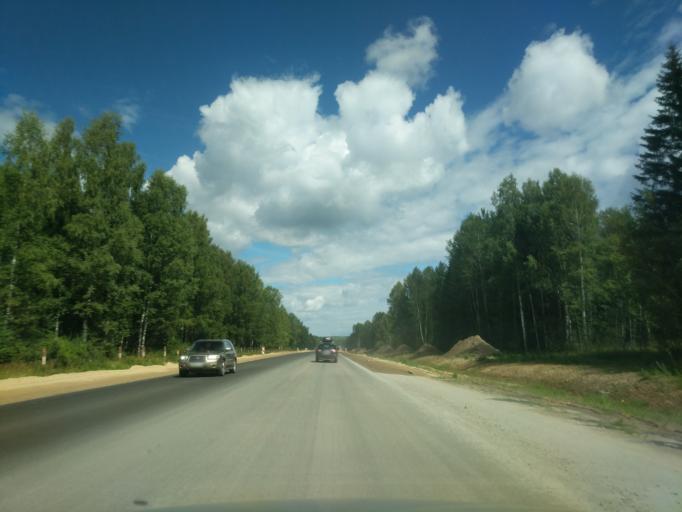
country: RU
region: Jaroslavl
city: Levashevo
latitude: 57.6606
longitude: 40.5685
